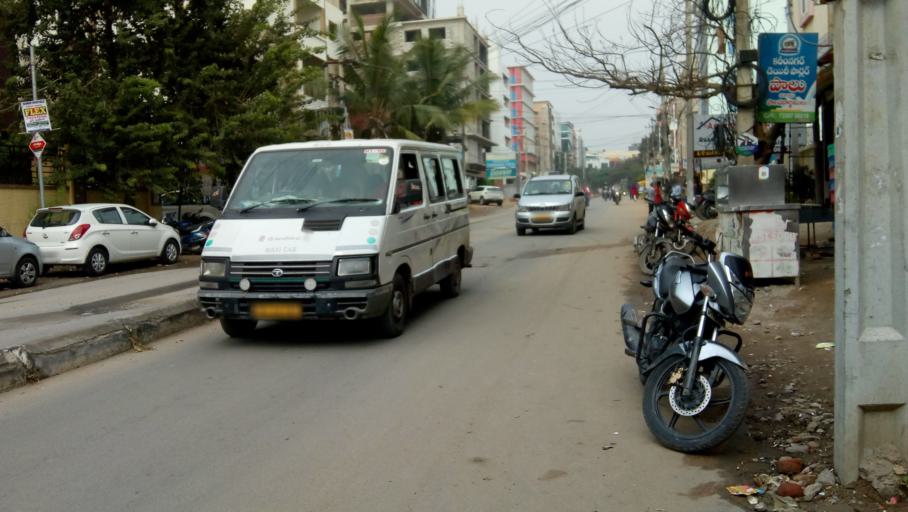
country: IN
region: Telangana
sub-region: Rangareddi
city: Kukatpalli
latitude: 17.4474
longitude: 78.3887
